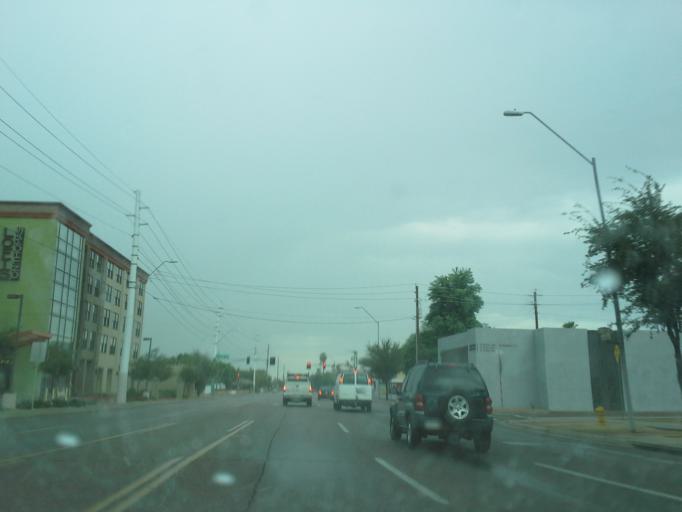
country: US
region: Arizona
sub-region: Maricopa County
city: Phoenix
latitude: 33.4803
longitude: -112.0813
